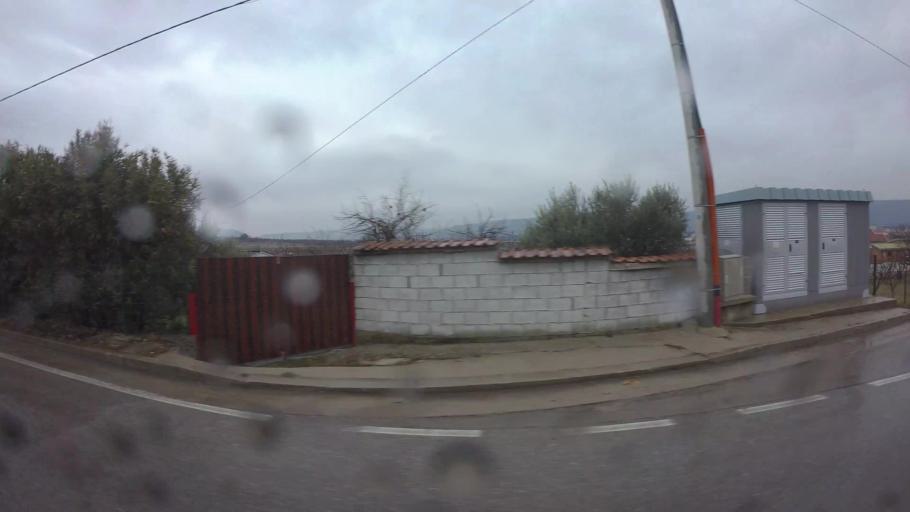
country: BA
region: Federation of Bosnia and Herzegovina
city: Blagaj
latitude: 43.2899
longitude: 17.8598
